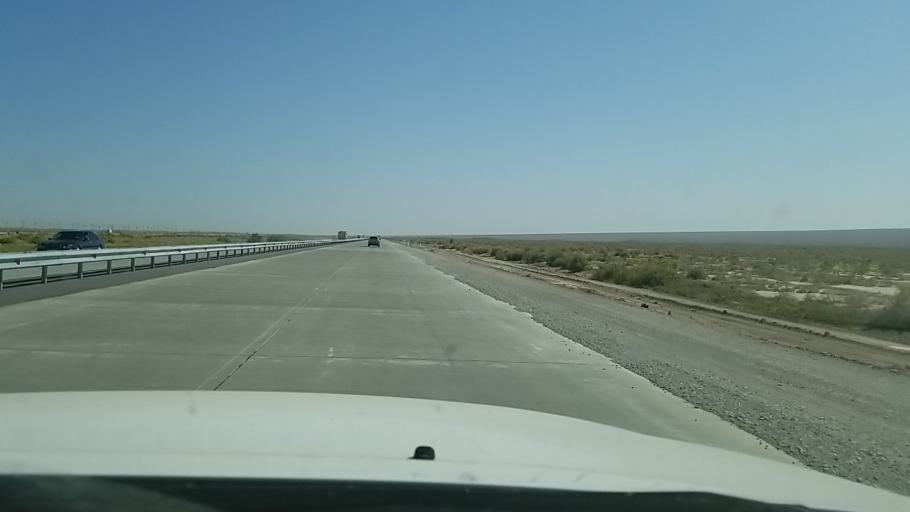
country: KZ
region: Almaty Oblysy
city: Kegen
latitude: 43.7479
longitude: 78.8750
